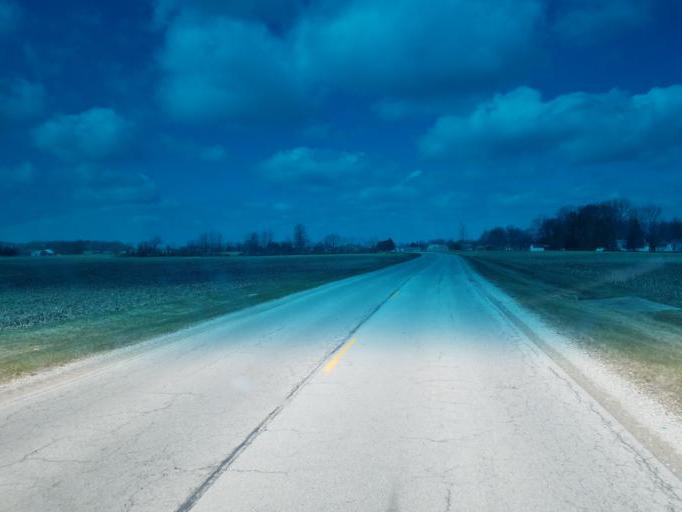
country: US
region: Ohio
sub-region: Crawford County
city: Bucyrus
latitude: 40.7893
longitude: -82.9508
